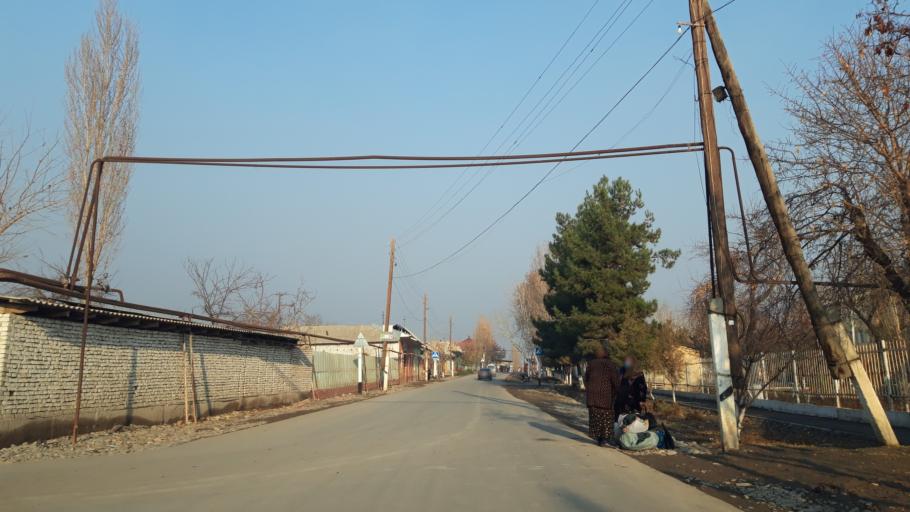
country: UZ
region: Andijon
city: Asaka
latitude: 40.6773
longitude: 72.1902
